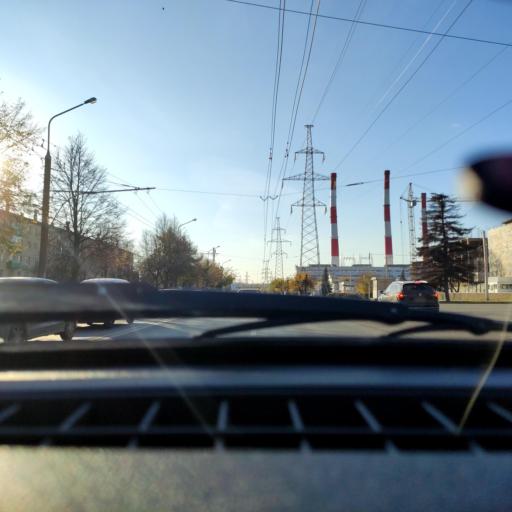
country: RU
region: Bashkortostan
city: Ufa
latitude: 54.7886
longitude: 56.1307
